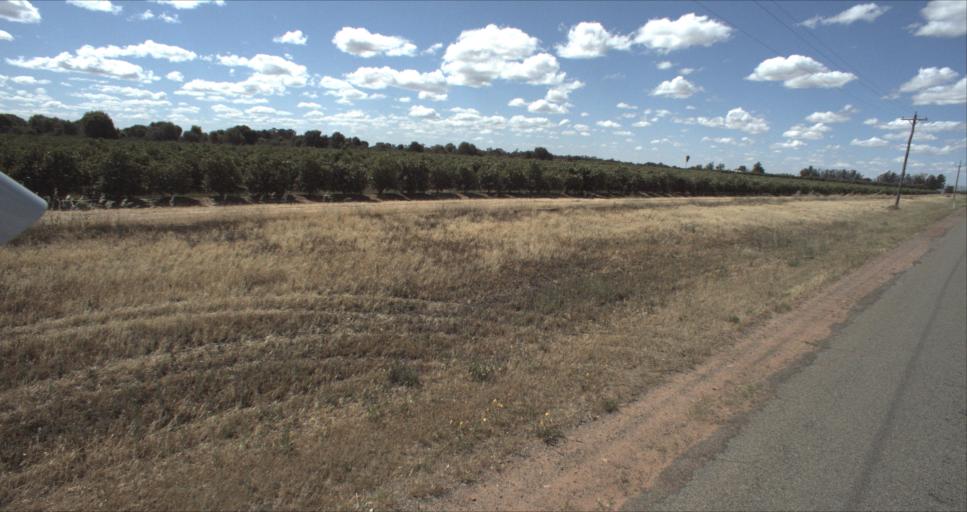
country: AU
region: New South Wales
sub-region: Leeton
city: Leeton
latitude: -34.5160
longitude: 146.2375
